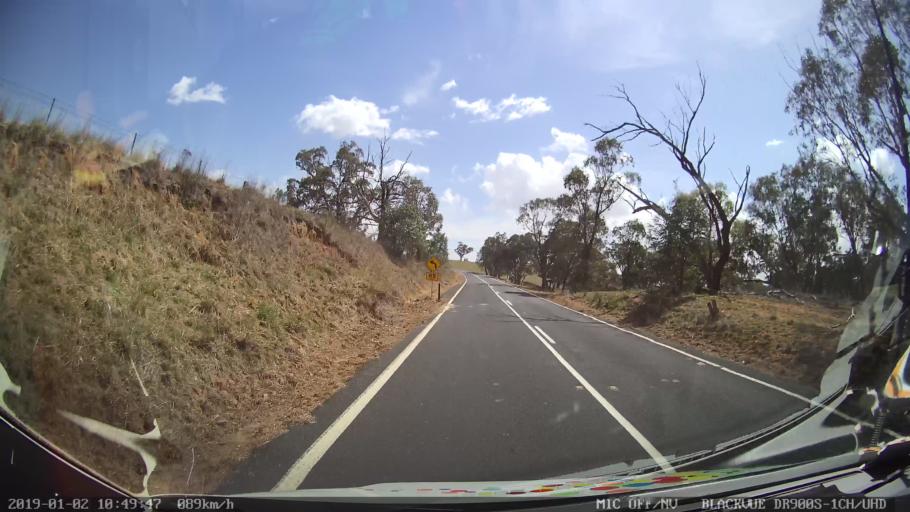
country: AU
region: New South Wales
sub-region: Cootamundra
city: Cootamundra
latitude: -34.7201
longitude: 148.2764
